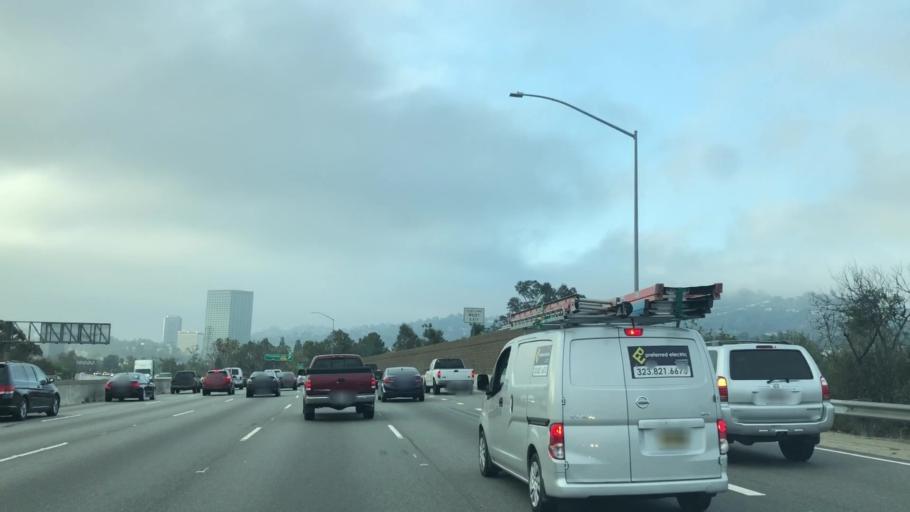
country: US
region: California
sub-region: Los Angeles County
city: Universal City
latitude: 34.1496
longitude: -118.3738
